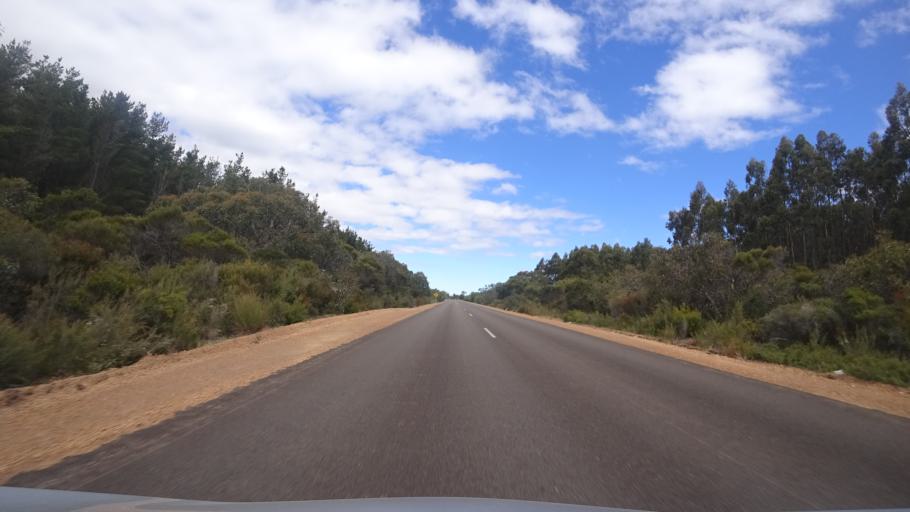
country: AU
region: South Australia
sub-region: Kangaroo Island
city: Kingscote
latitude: -35.7937
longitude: 137.0207
